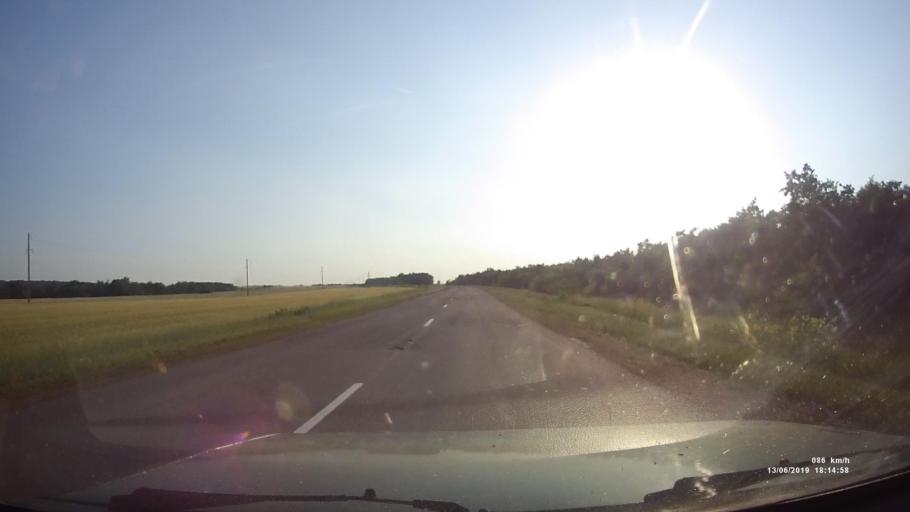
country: RU
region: Rostov
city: Kazanskaya
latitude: 49.9328
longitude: 41.3657
